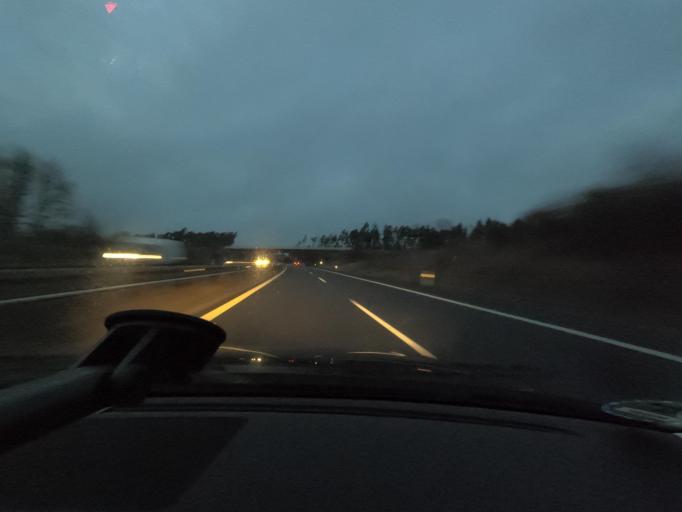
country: DE
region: Bavaria
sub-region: Upper Franconia
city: Lautertal
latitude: 50.3136
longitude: 10.9609
